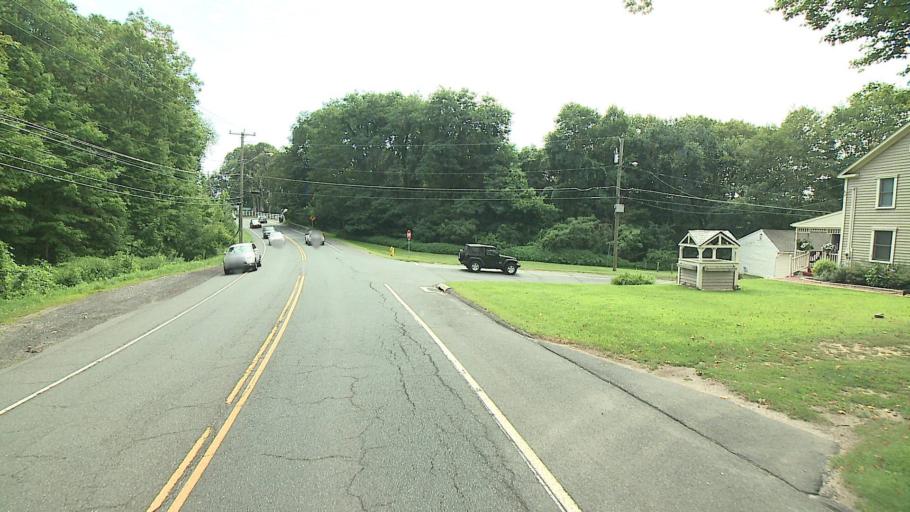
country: US
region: Connecticut
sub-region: Fairfield County
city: Danbury
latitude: 41.4224
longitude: -73.4813
